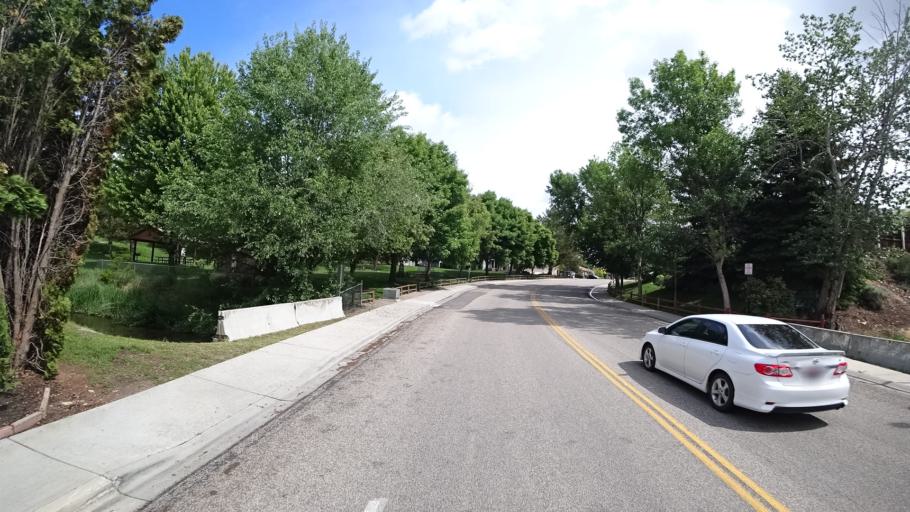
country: US
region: Idaho
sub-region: Ada County
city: Eagle
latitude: 43.6987
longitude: -116.3496
